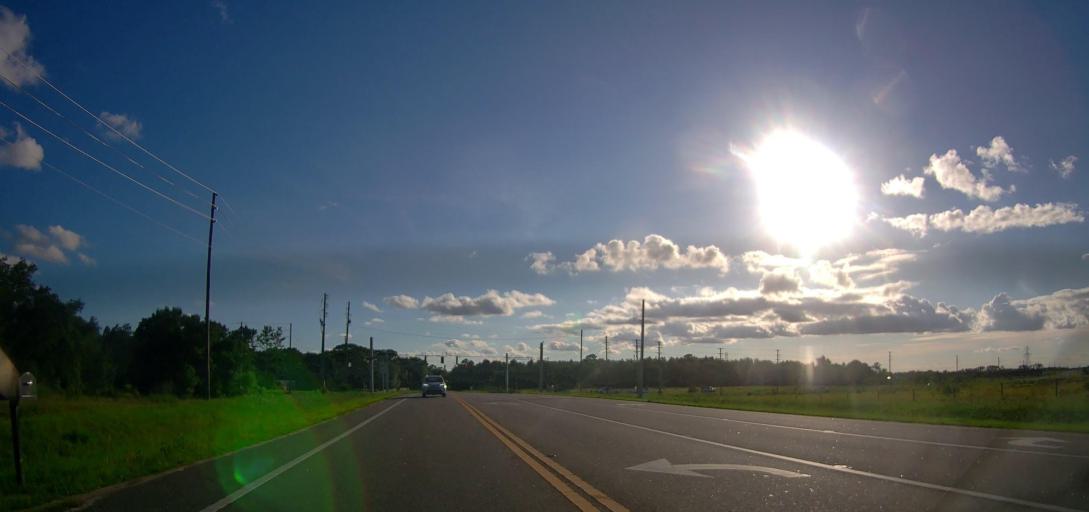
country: US
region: Florida
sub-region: Marion County
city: Silver Springs Shores
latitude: 29.0642
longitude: -82.0165
